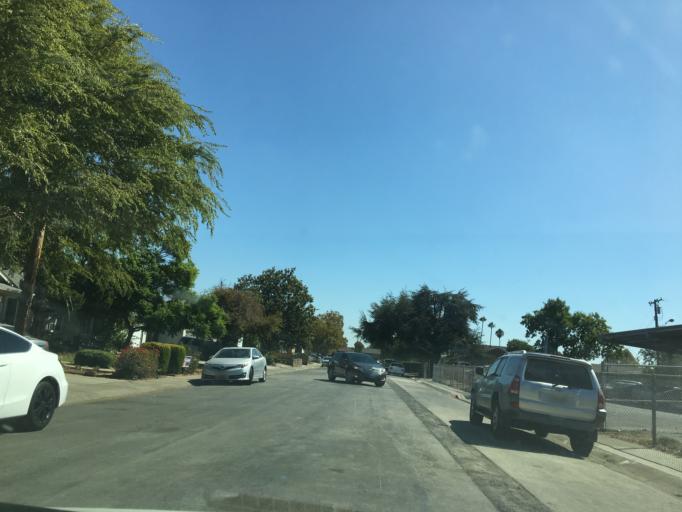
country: US
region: California
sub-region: Santa Clara County
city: East Foothills
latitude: 37.3907
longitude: -121.8378
